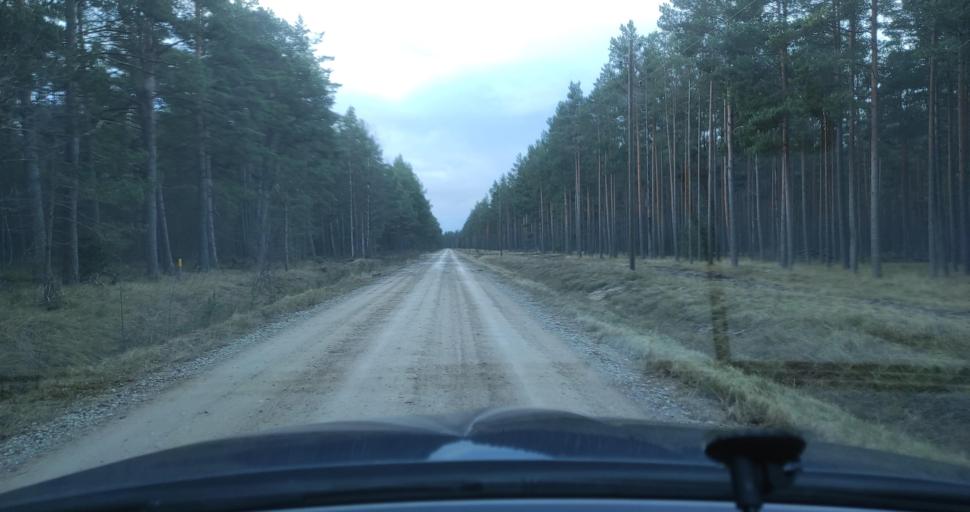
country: LV
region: Pavilostas
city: Pavilosta
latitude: 56.8023
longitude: 21.0668
